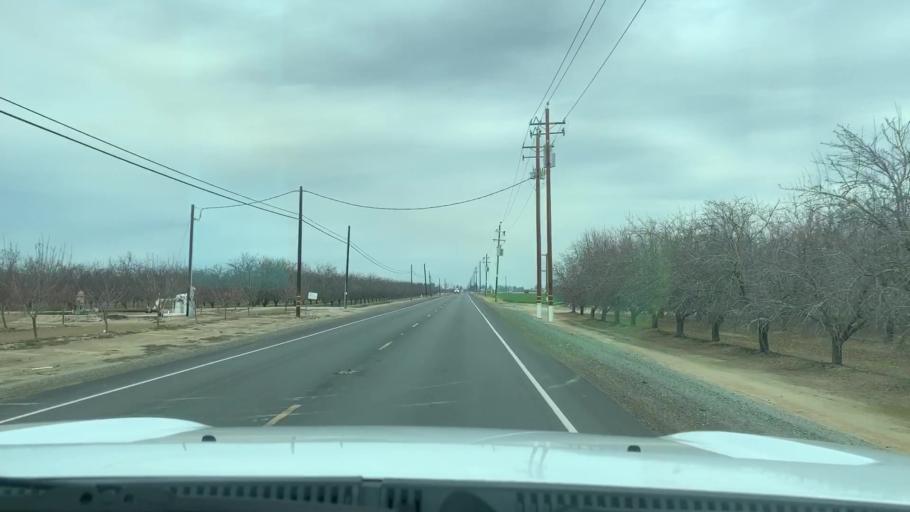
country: US
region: California
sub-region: Kern County
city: Shafter
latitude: 35.4048
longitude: -119.2520
